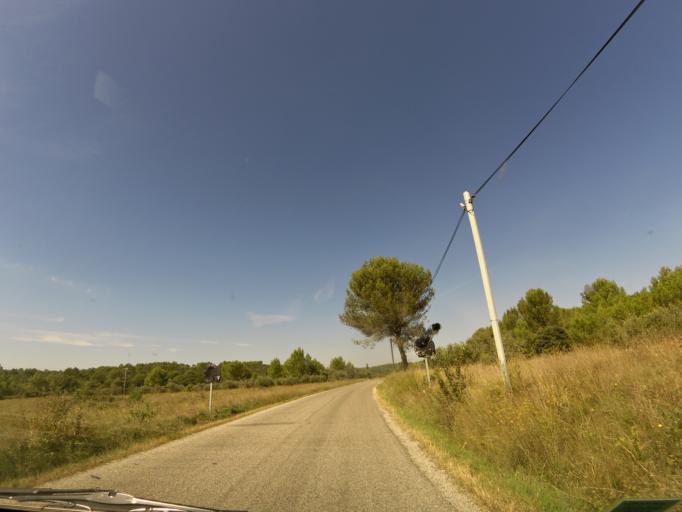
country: FR
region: Languedoc-Roussillon
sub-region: Departement du Gard
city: Uchaud
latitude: 43.7622
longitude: 4.2561
